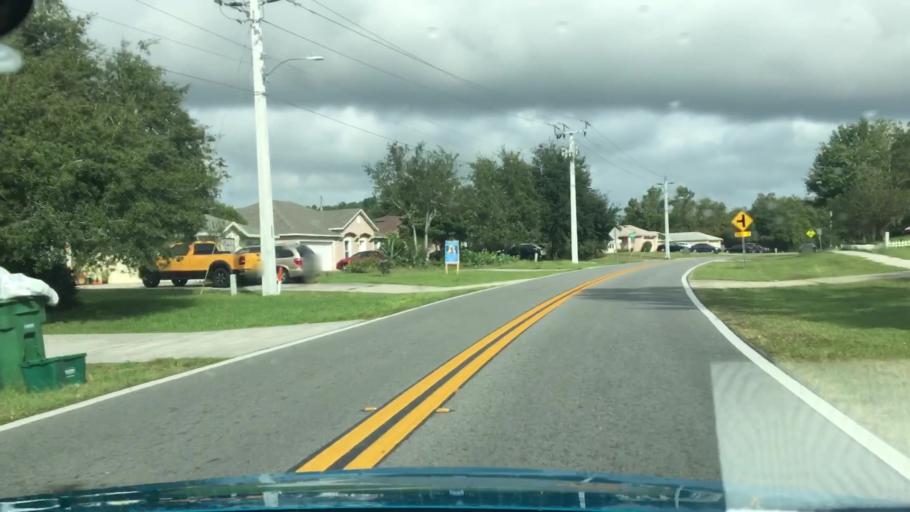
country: US
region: Florida
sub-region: Volusia County
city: Lake Helen
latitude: 28.9509
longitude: -81.1865
